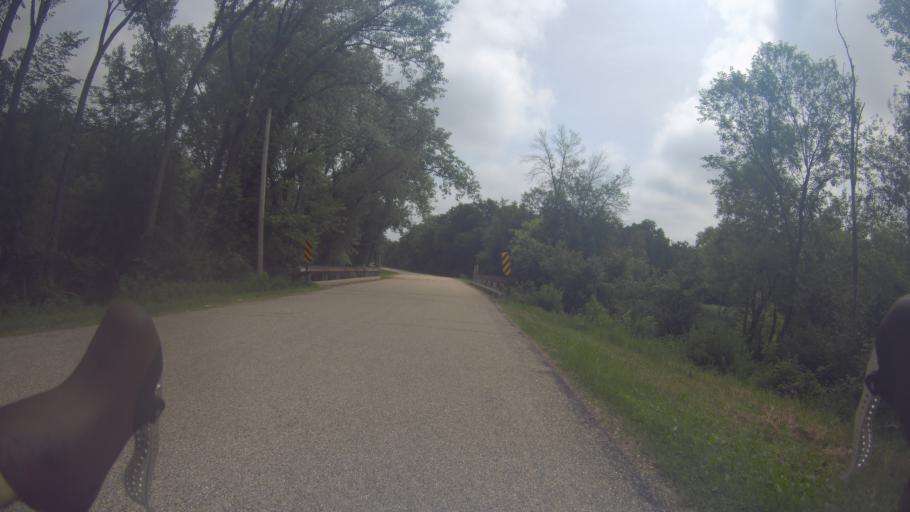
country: US
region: Wisconsin
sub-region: Jefferson County
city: Cambridge
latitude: 42.9207
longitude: -89.0284
